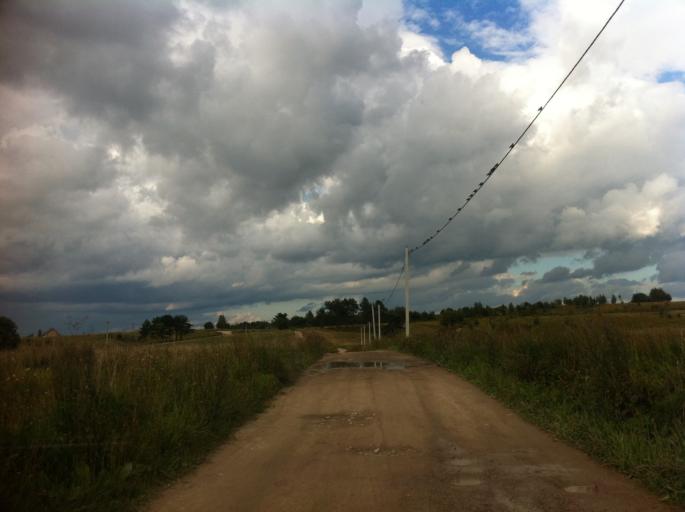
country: RU
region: Pskov
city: Izborsk
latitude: 57.8205
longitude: 27.9625
